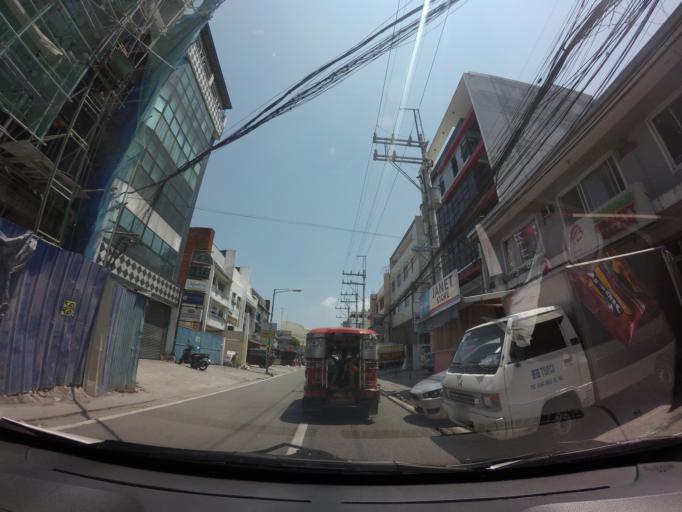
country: PH
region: Metro Manila
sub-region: Makati City
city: Makati City
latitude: 14.5573
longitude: 121.0036
